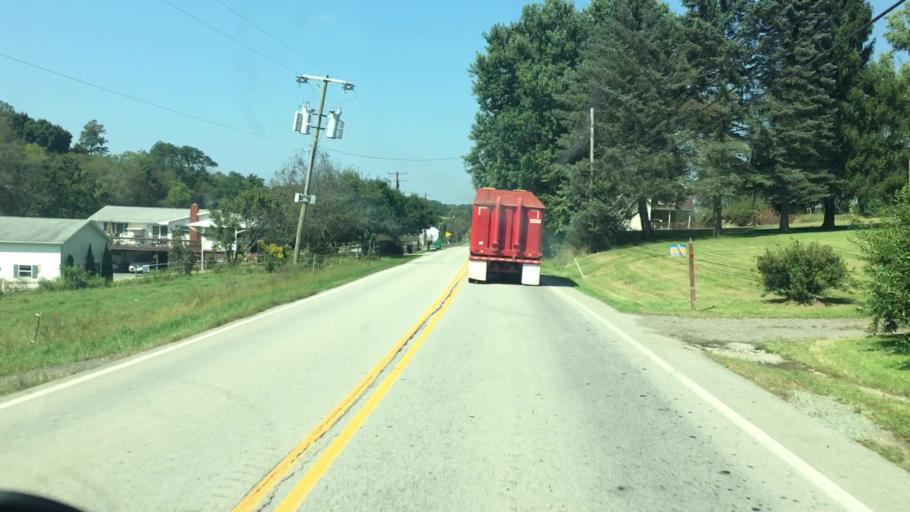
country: US
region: Pennsylvania
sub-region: Washington County
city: Washington
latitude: 40.1009
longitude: -80.2887
